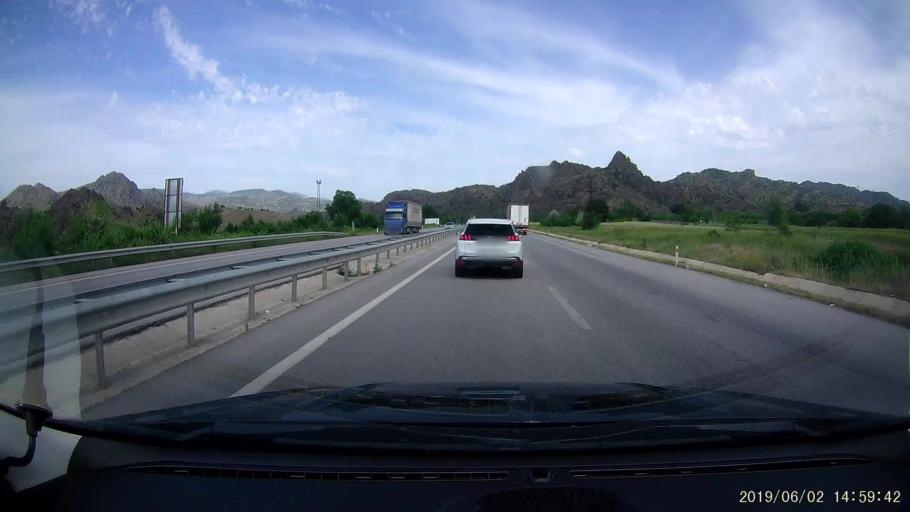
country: TR
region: Corum
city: Osmancik
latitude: 40.9717
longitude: 34.6995
